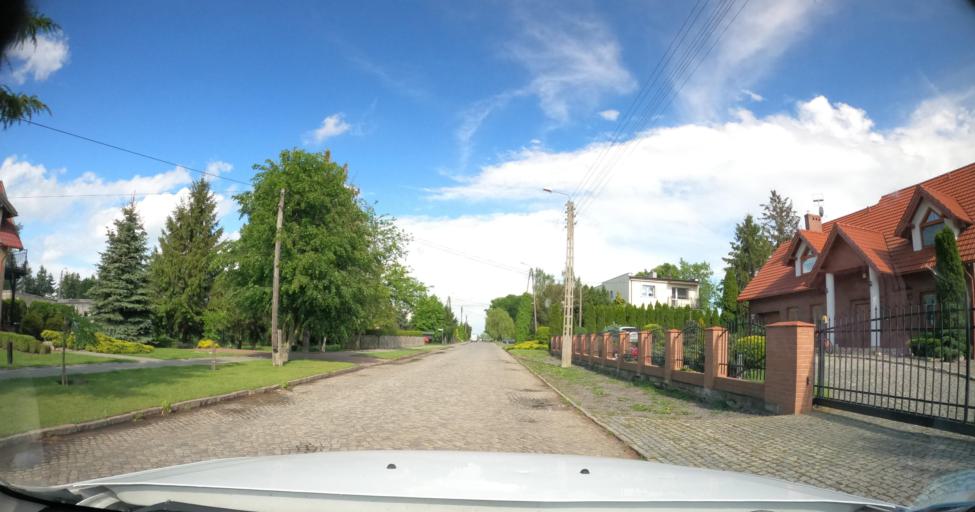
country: PL
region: Pomeranian Voivodeship
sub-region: Powiat nowodworski
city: Nowy Dwor Gdanski
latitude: 54.1890
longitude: 19.1545
